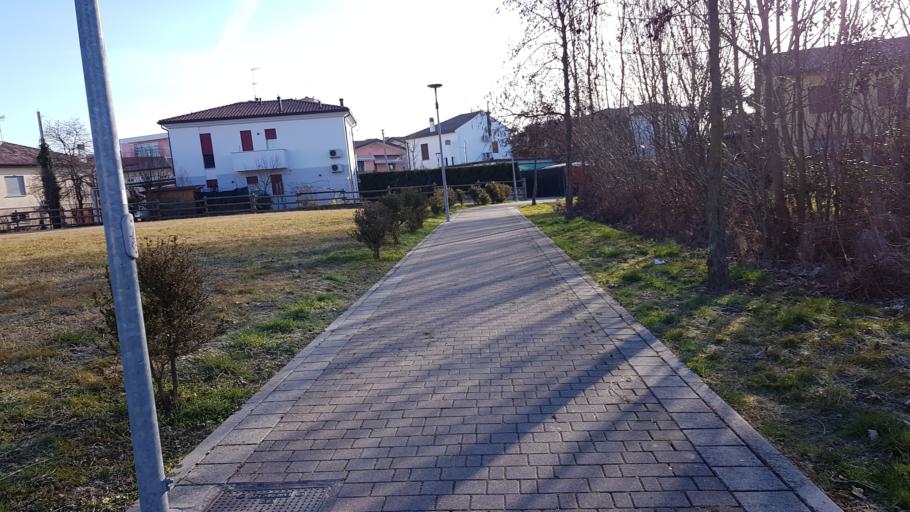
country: IT
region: Veneto
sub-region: Provincia di Padova
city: San Giorgio delle Pertiche
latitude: 45.5413
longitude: 11.9080
